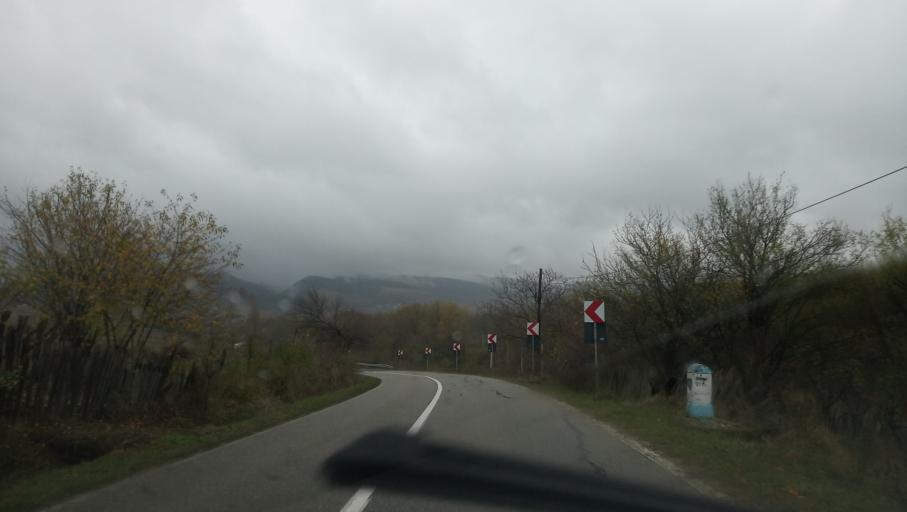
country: RO
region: Gorj
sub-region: Comuna Musetesti
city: Musetesti
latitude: 45.1538
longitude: 23.4618
